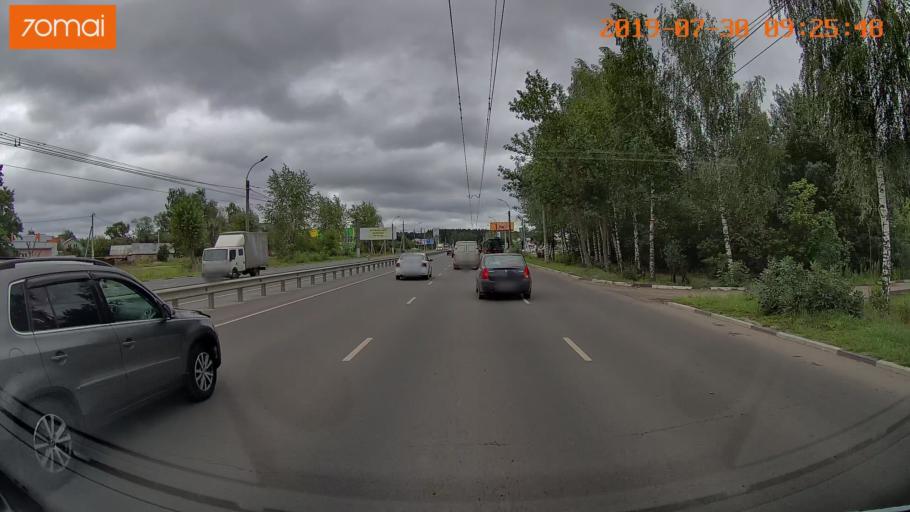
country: RU
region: Ivanovo
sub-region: Gorod Ivanovo
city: Ivanovo
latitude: 56.9502
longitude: 40.9751
